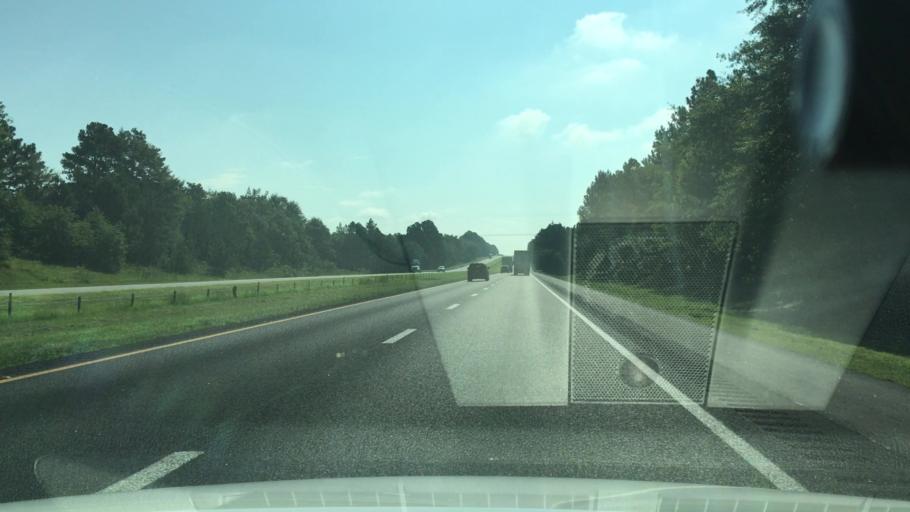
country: US
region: South Carolina
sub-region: Aiken County
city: Graniteville
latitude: 33.6339
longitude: -81.7793
